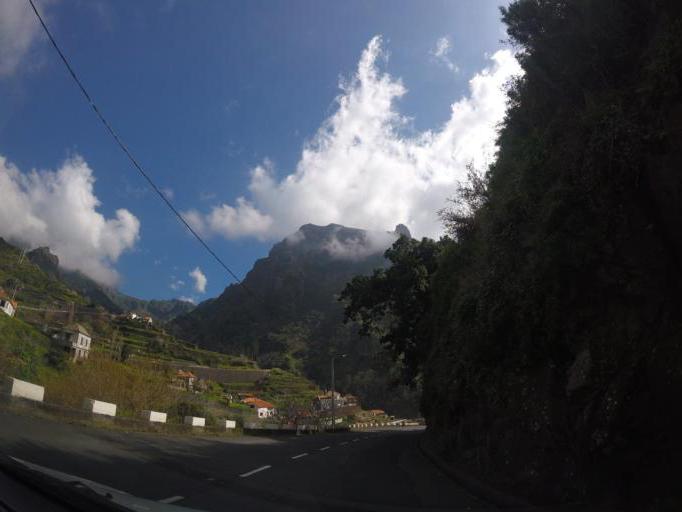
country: PT
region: Madeira
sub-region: Camara de Lobos
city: Curral das Freiras
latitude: 32.7288
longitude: -17.0291
